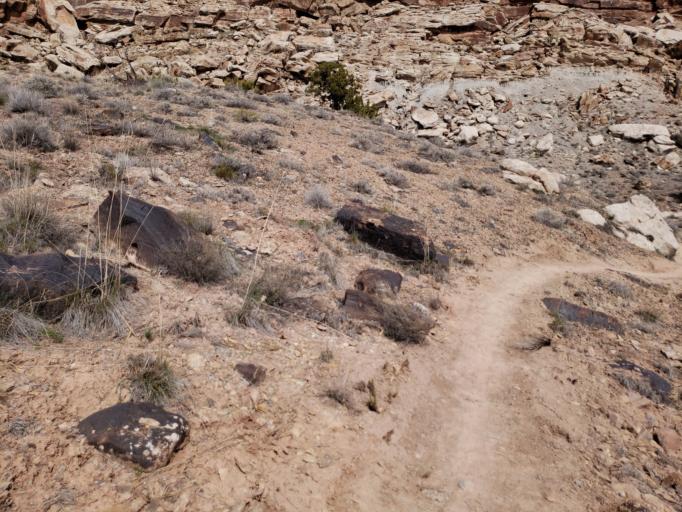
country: US
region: Colorado
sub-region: Mesa County
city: Loma
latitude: 39.1929
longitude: -108.8844
